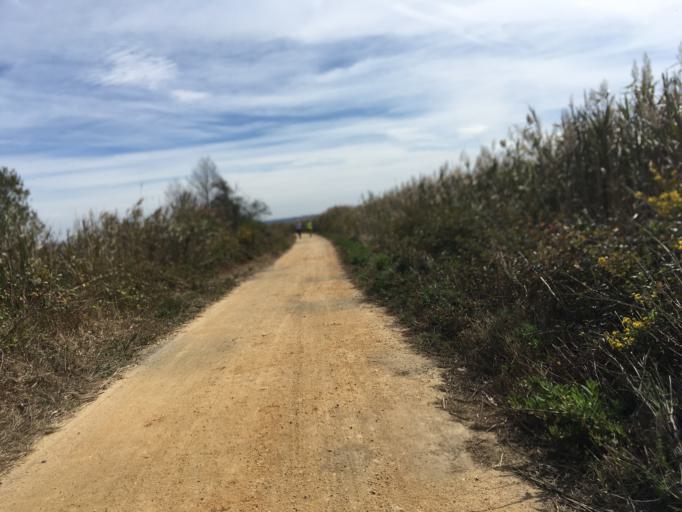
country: PT
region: Aveiro
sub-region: Murtosa
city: Murtosa
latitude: 40.7294
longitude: -8.6024
